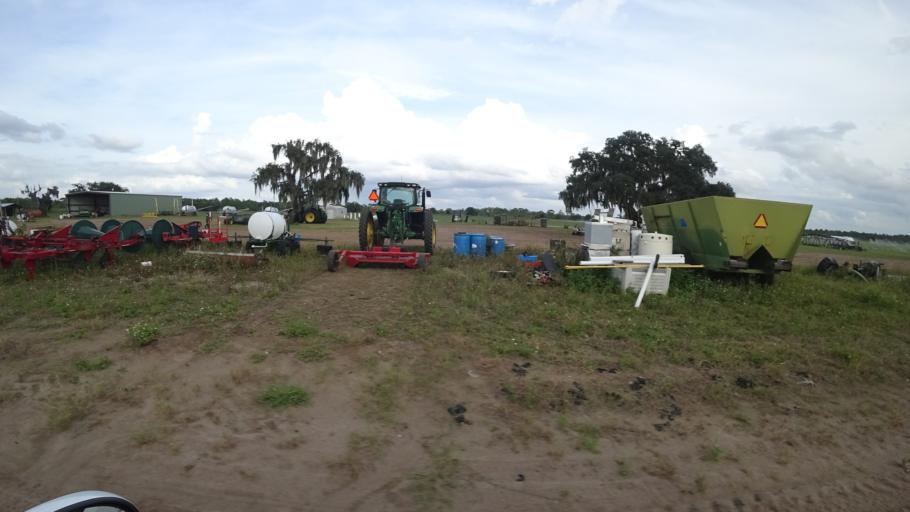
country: US
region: Florida
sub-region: Hillsborough County
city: Wimauma
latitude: 27.5770
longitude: -82.1573
